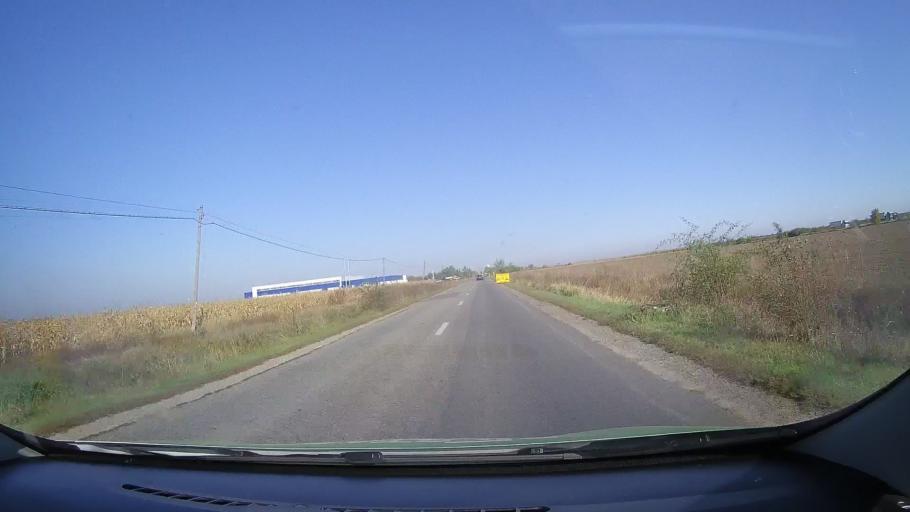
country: RO
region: Satu Mare
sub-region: Oras Tasnad
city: Tasnad
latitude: 47.5031
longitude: 22.5742
